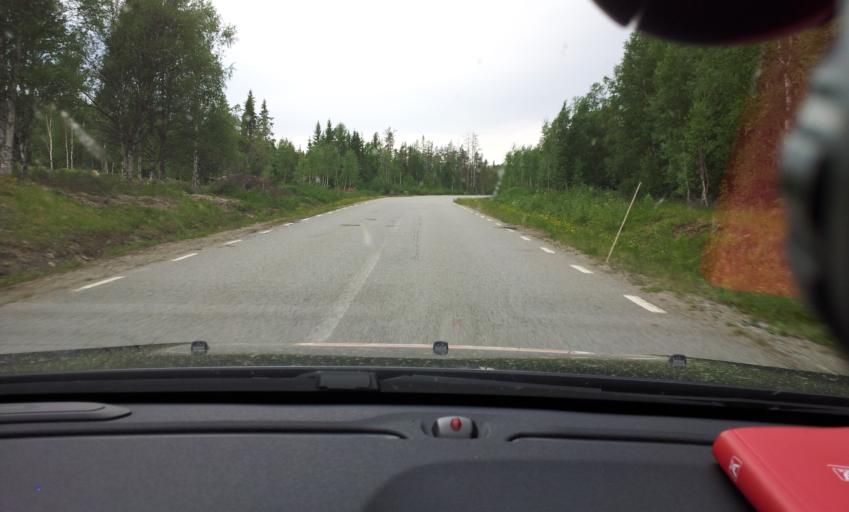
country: SE
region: Jaemtland
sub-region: Bergs Kommun
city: Hoverberg
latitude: 62.6841
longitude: 14.6409
